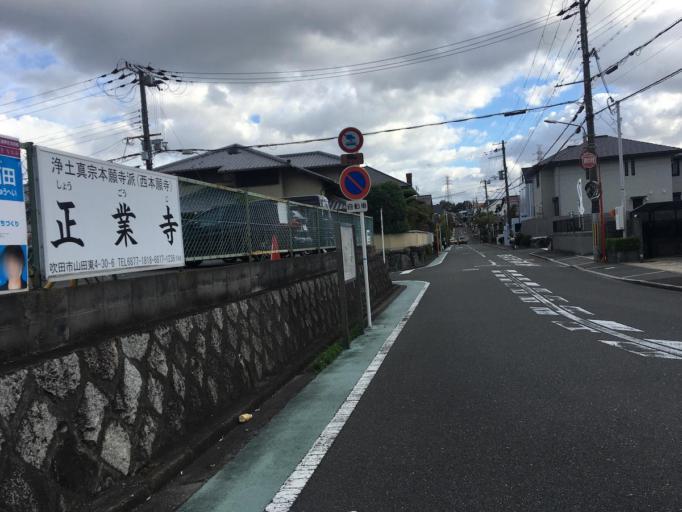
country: JP
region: Osaka
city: Suita
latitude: 34.8028
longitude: 135.5160
